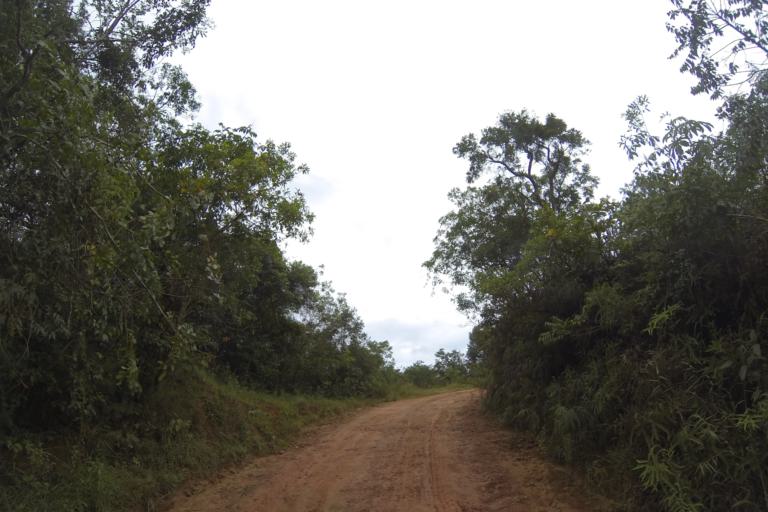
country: BR
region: Minas Gerais
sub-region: Ibia
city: Ibia
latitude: -19.7405
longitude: -46.5473
